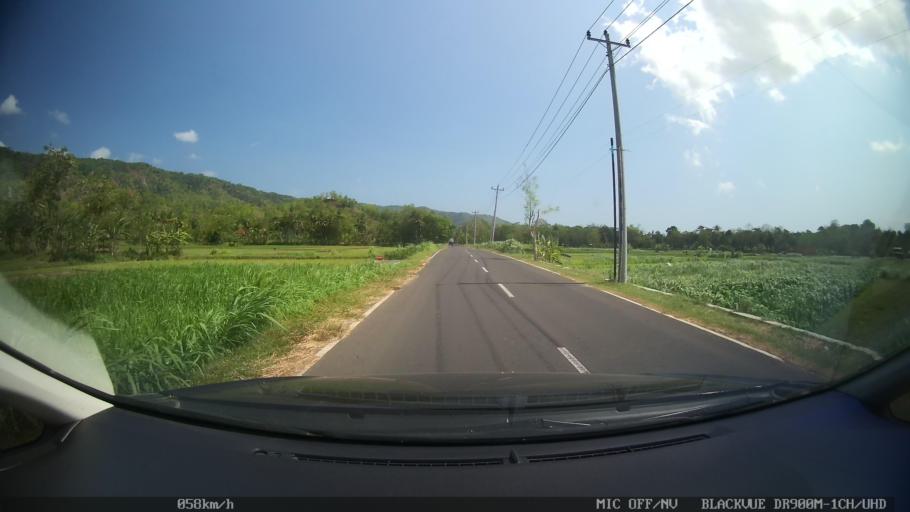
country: ID
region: Daerah Istimewa Yogyakarta
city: Pundong
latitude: -7.9703
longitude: 110.3510
